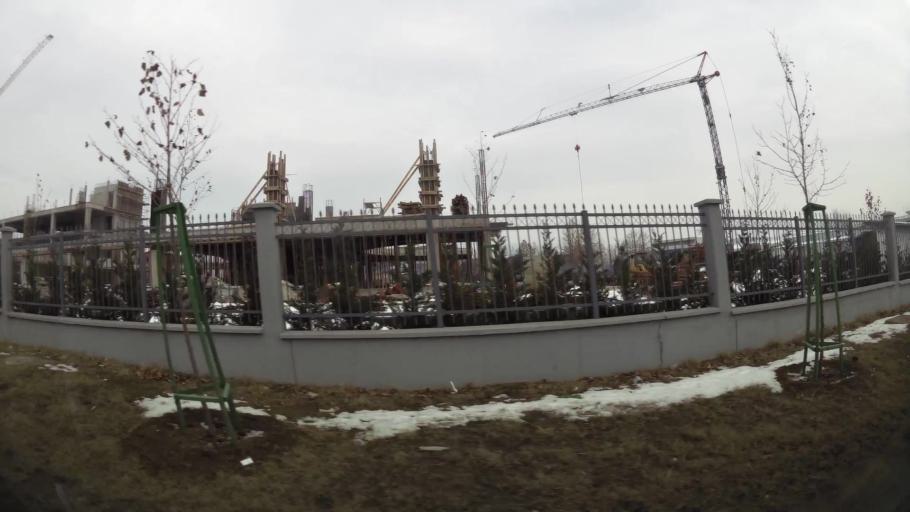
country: MK
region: Suto Orizari
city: Suto Orizare
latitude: 42.0449
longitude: 21.3885
